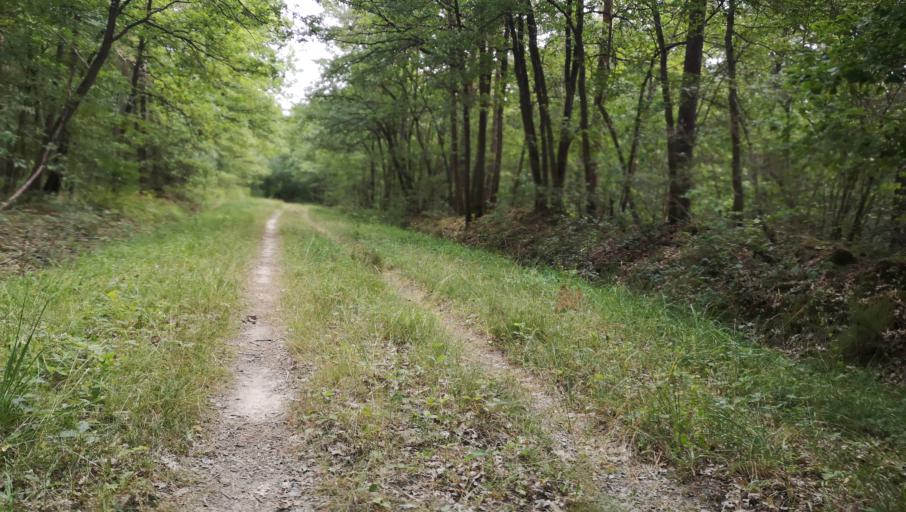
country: FR
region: Centre
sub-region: Departement du Loiret
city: Semoy
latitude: 47.9519
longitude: 1.9443
